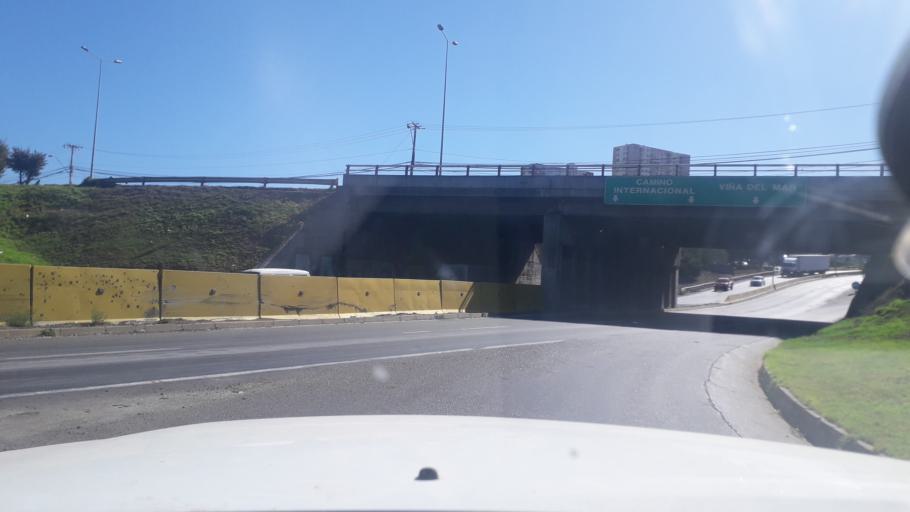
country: CL
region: Valparaiso
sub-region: Provincia de Valparaiso
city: Vina del Mar
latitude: -33.0368
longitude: -71.5003
